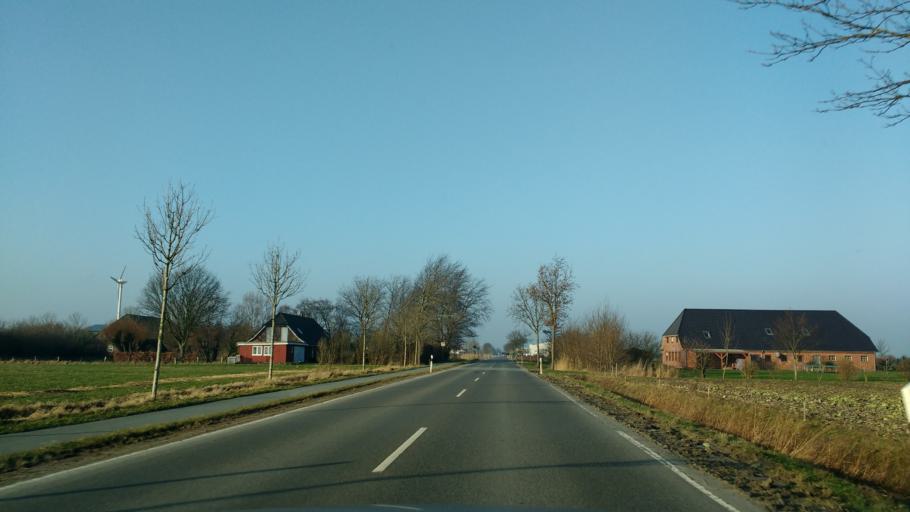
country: DE
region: Schleswig-Holstein
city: Friedrichskoog
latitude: 53.9927
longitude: 8.9005
